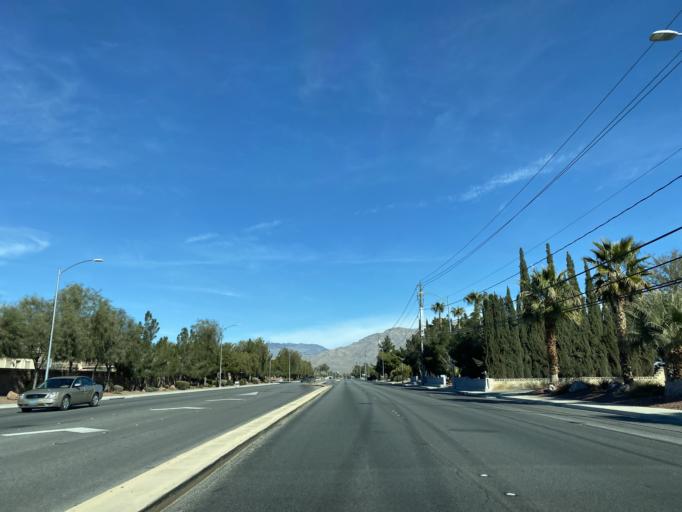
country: US
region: Nevada
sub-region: Clark County
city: North Las Vegas
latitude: 36.2910
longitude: -115.2242
